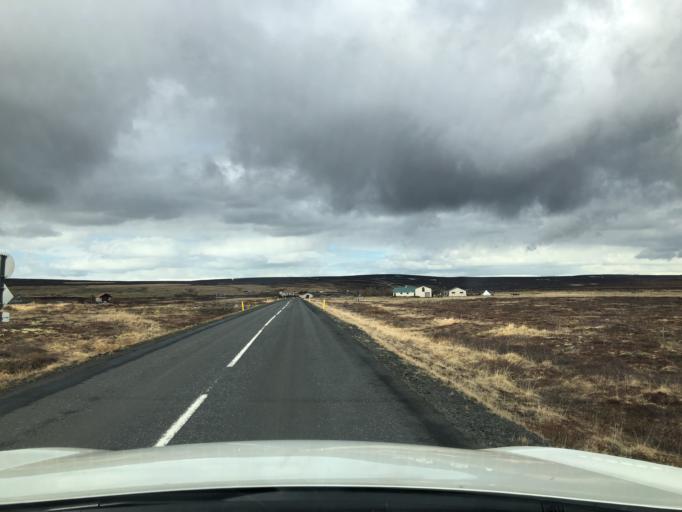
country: IS
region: Northeast
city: Laugar
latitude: 65.5831
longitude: -17.1182
